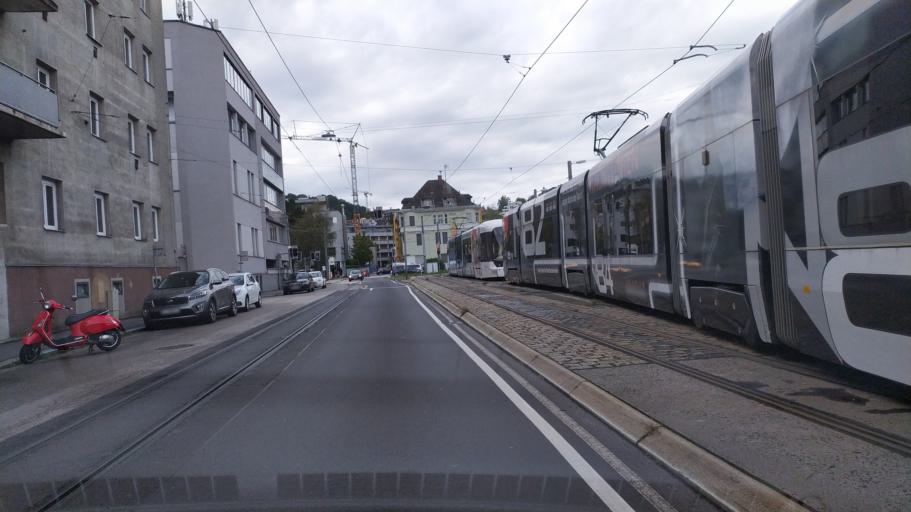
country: AT
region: Upper Austria
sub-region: Linz Stadt
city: Linz
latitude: 48.3113
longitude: 14.2785
